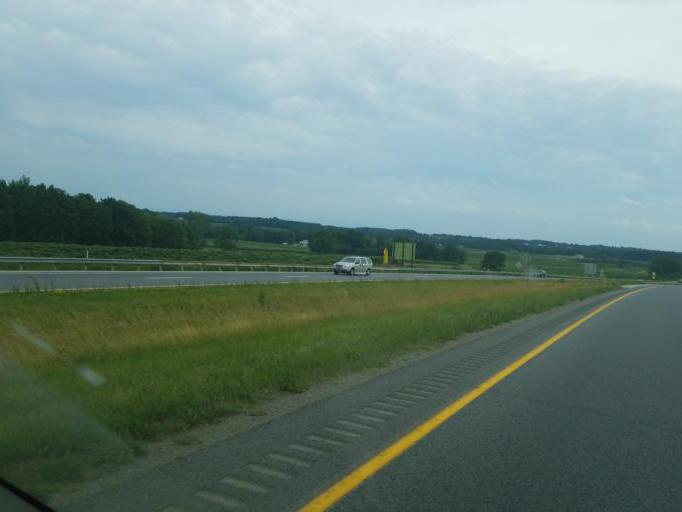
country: US
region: Pennsylvania
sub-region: Erie County
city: North East
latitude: 42.2282
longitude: -79.7822
